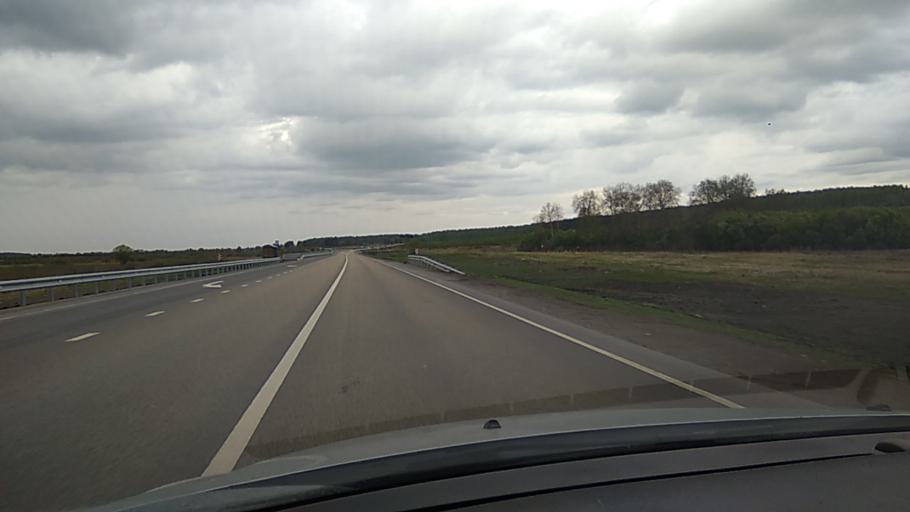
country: RU
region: Kurgan
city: Kataysk
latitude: 56.2972
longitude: 62.4174
